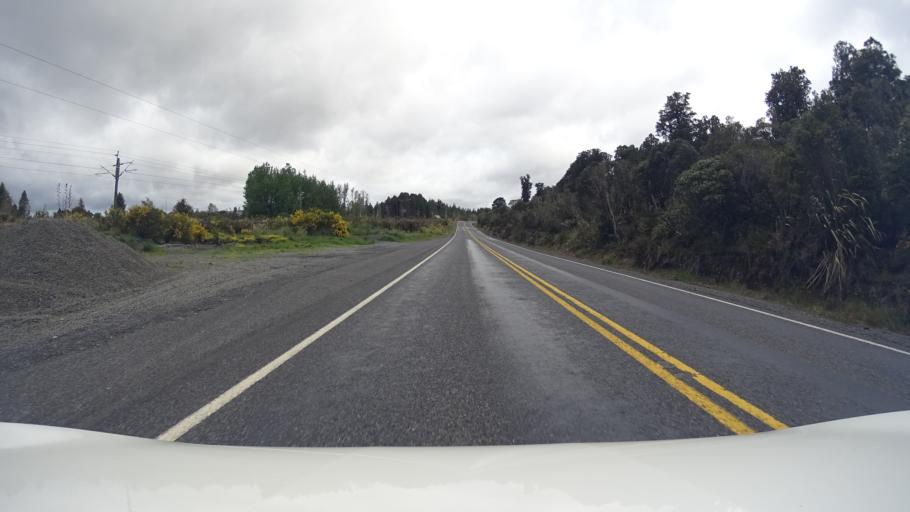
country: NZ
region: Manawatu-Wanganui
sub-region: Ruapehu District
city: Waiouru
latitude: -39.2576
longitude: 175.3883
